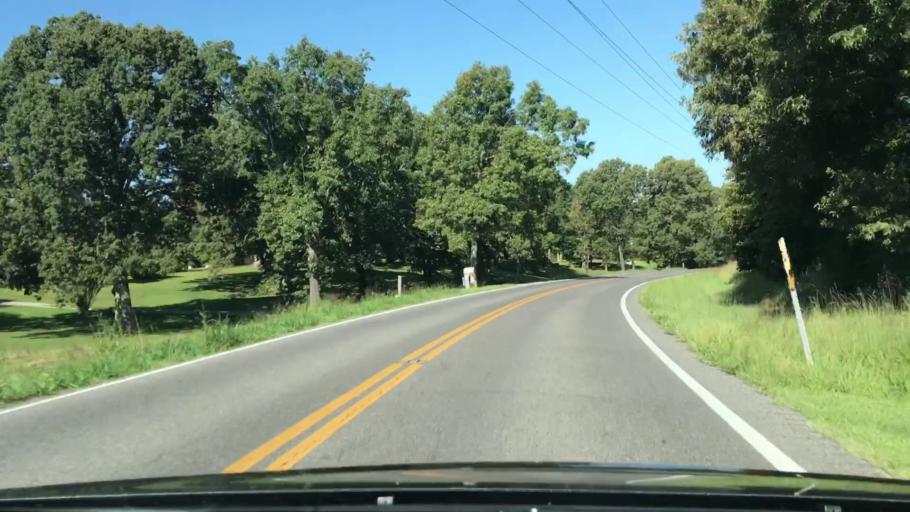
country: US
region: Kentucky
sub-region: Graves County
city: Mayfield
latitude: 36.7730
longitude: -88.4995
